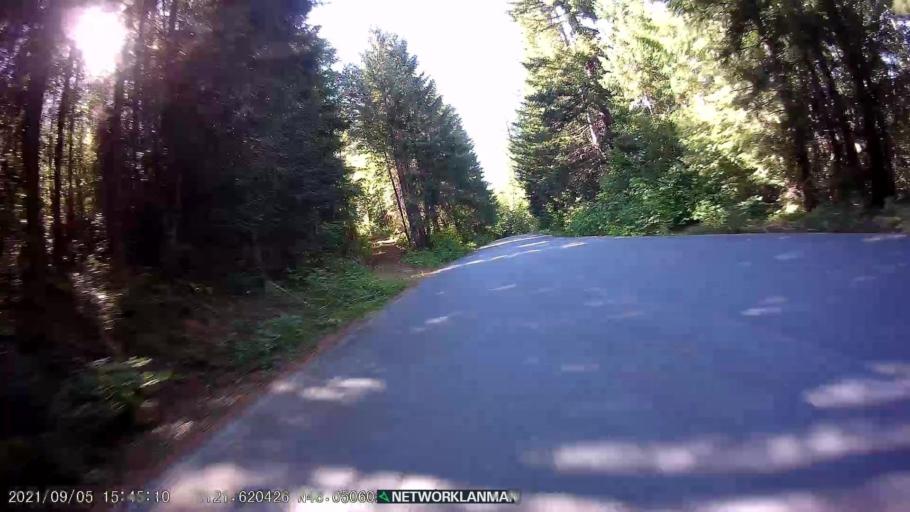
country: US
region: Washington
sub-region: Klickitat County
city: White Salmon
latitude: 46.0505
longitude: -121.6201
